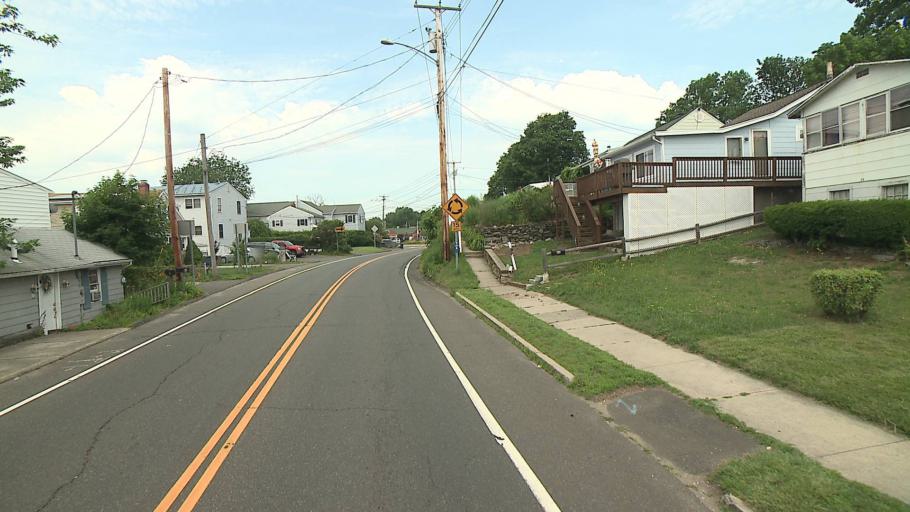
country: US
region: Connecticut
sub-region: New Haven County
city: Woodmont
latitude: 41.2361
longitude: -72.9845
